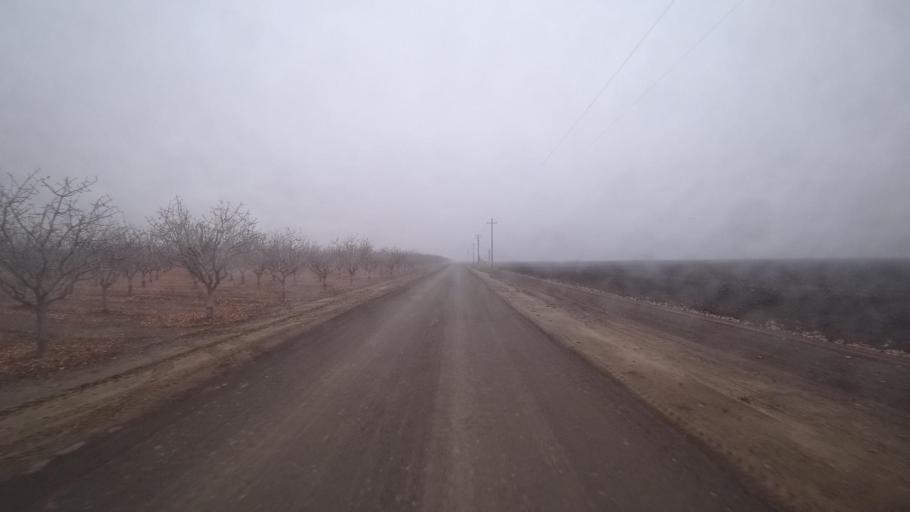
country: US
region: California
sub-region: Kern County
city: Buttonwillow
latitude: 35.4268
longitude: -119.5541
